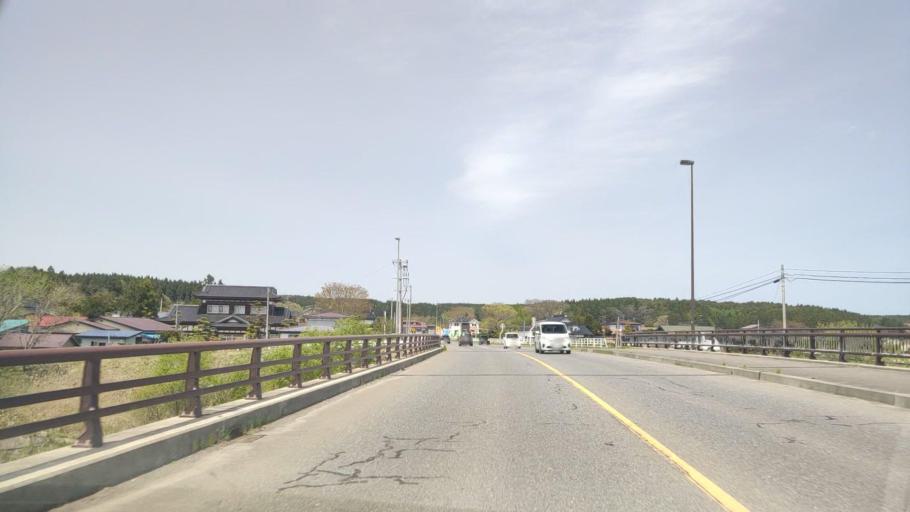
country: JP
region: Aomori
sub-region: Misawa Shi
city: Inuotose
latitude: 40.5566
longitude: 141.3883
